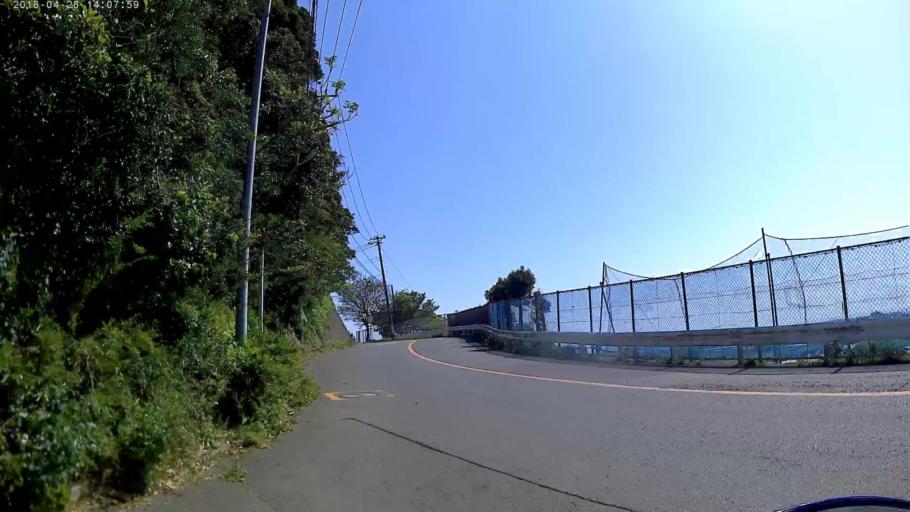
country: JP
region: Kanagawa
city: Miura
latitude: 35.1513
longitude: 139.6466
